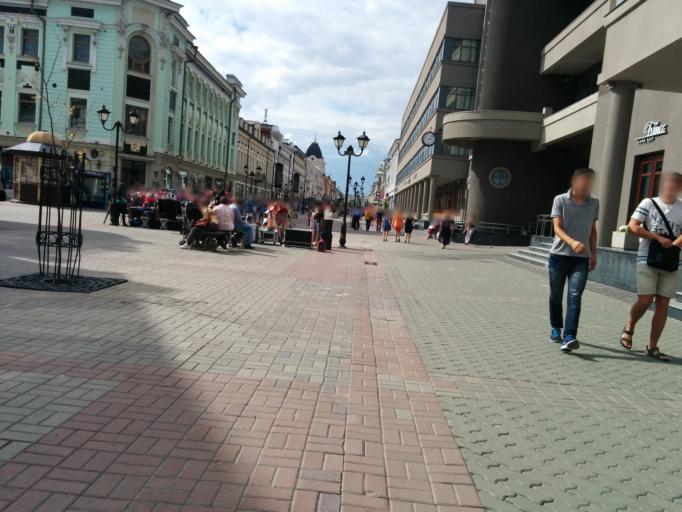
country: RU
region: Tatarstan
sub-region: Gorod Kazan'
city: Kazan
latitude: 55.7907
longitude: 49.1150
